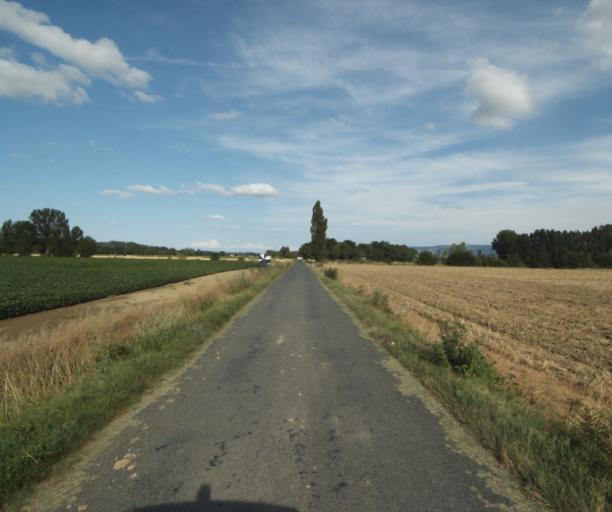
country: FR
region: Midi-Pyrenees
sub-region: Departement du Tarn
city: Puylaurens
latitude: 43.5199
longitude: 1.9929
